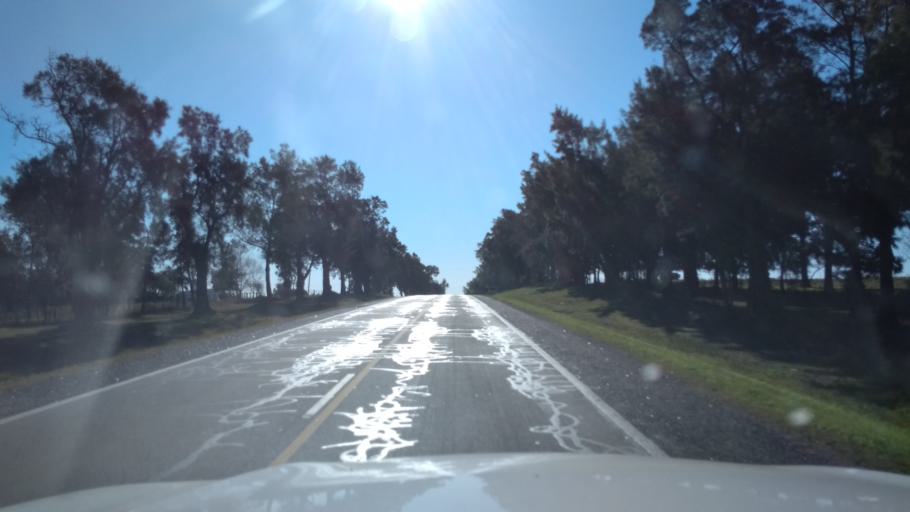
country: UY
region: Canelones
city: San Jacinto
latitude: -34.5906
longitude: -55.8360
